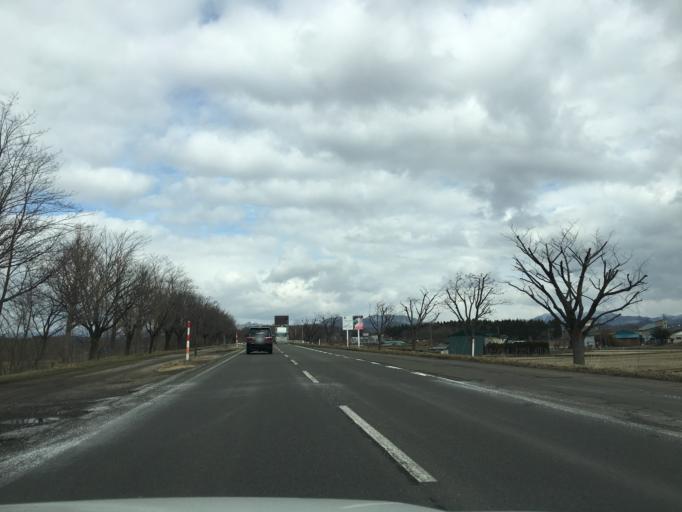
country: JP
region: Akita
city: Hanawa
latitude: 40.2576
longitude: 140.7622
